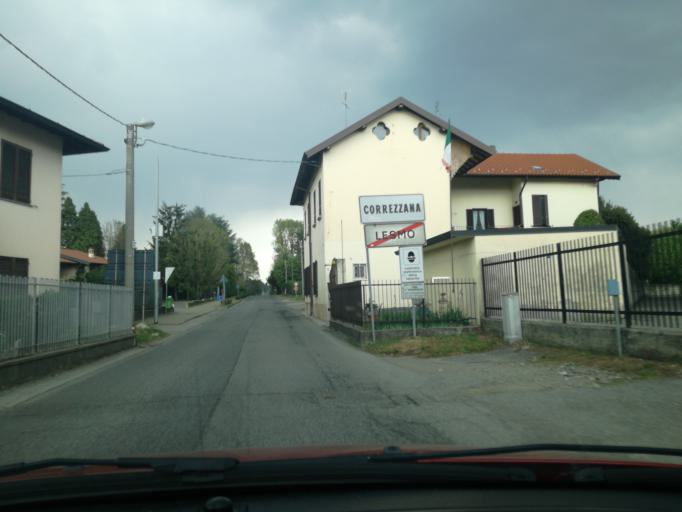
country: IT
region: Lombardy
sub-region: Provincia di Monza e Brianza
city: Lesmo
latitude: 45.6539
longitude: 9.3059
